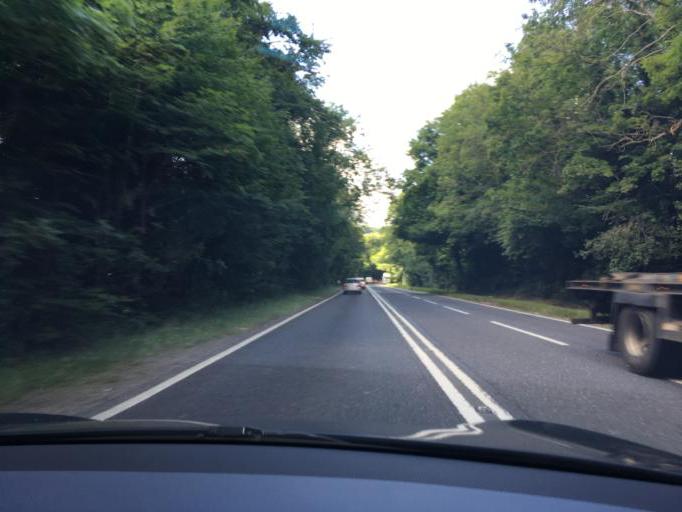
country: GB
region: England
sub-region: Surrey
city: Leatherhead
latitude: 51.2833
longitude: -0.3210
